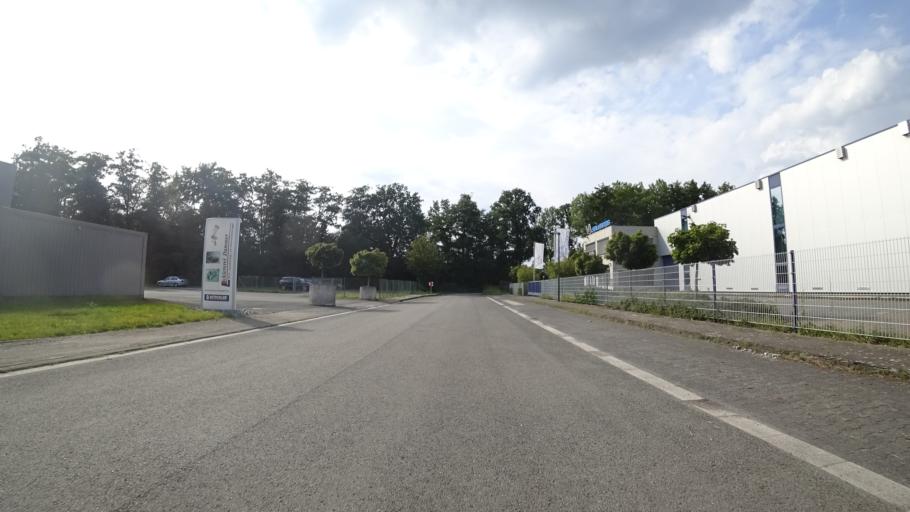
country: DE
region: North Rhine-Westphalia
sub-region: Regierungsbezirk Detmold
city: Guetersloh
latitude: 51.9427
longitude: 8.4340
